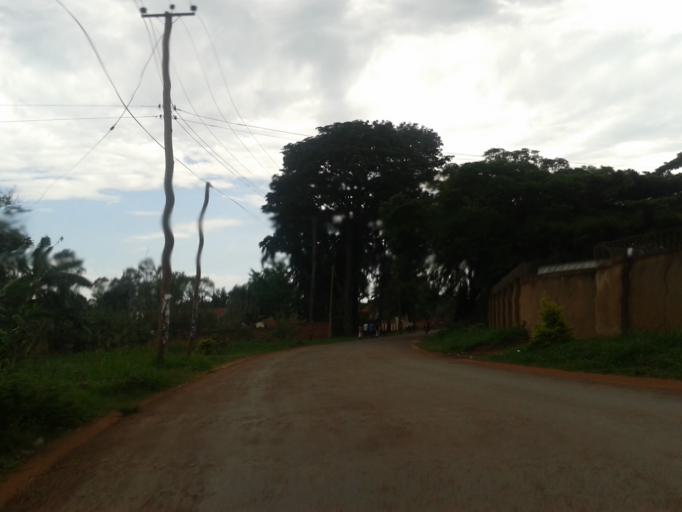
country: UG
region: Northern Region
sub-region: Gulu District
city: Gulu
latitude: 2.7815
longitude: 32.3052
